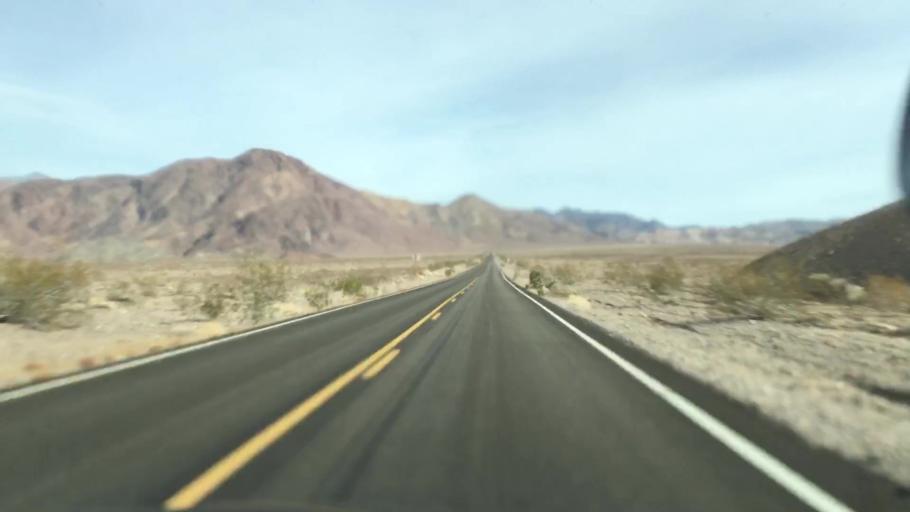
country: US
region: Nevada
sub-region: Nye County
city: Beatty
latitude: 36.6780
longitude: -117.0093
